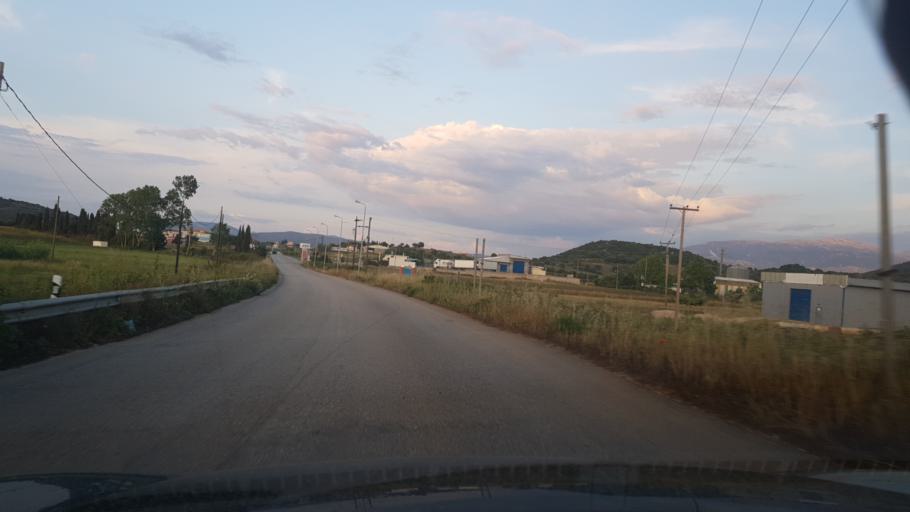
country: GR
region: Ionian Islands
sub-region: Lefkada
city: Lefkada
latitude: 38.8632
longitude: 20.7885
